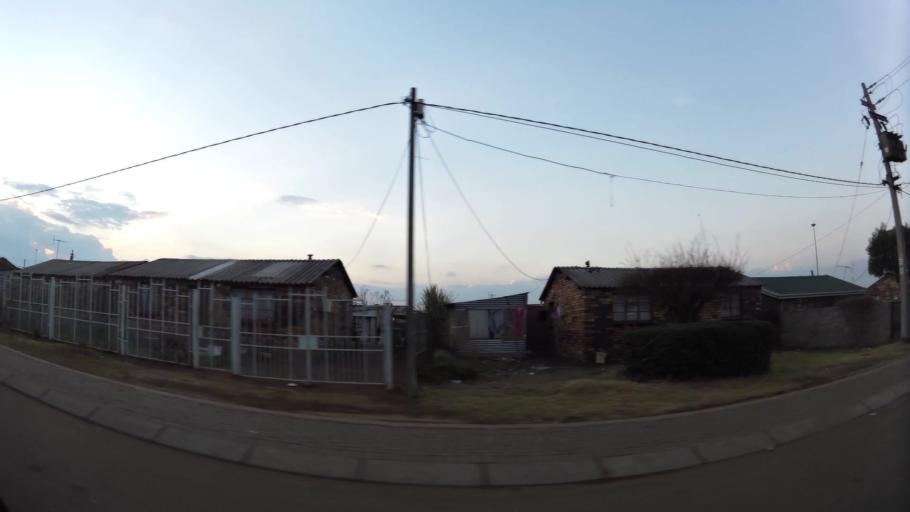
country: ZA
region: Gauteng
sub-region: City of Johannesburg Metropolitan Municipality
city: Orange Farm
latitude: -26.5566
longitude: 27.8726
